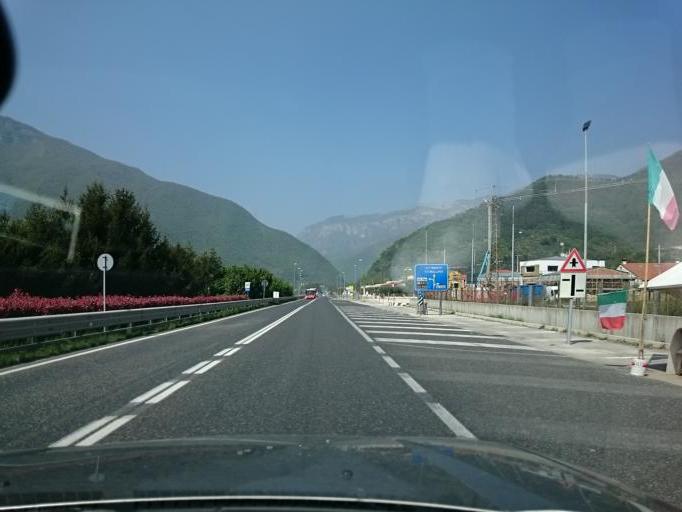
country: IT
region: Veneto
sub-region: Provincia di Vicenza
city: Pove del Grappa
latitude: 45.7959
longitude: 11.7225
